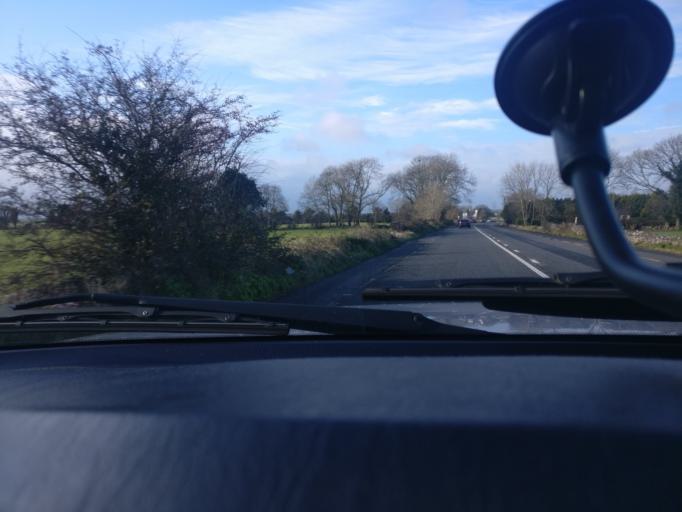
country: IE
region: Connaught
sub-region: County Galway
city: Oranmore
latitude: 53.2737
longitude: -8.8487
